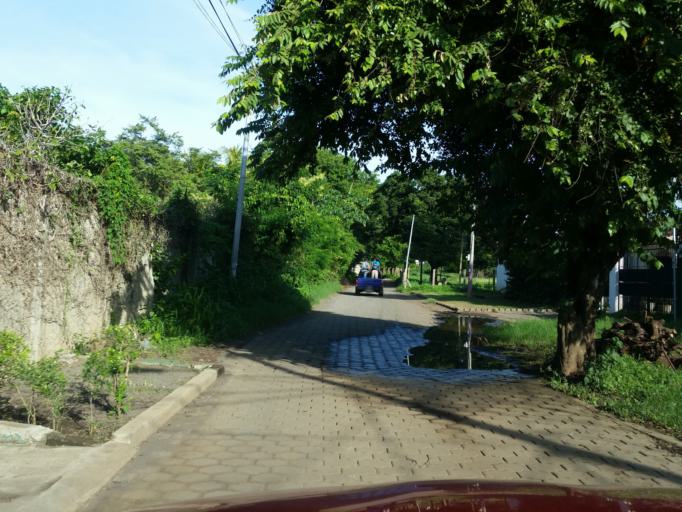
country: NI
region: Masaya
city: Ticuantepe
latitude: 12.0735
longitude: -86.2265
